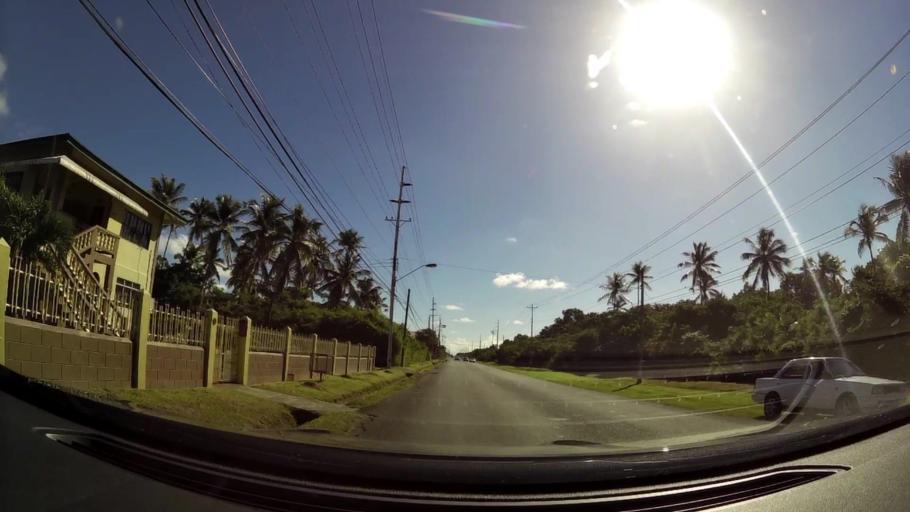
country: TT
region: Tobago
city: Scarborough
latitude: 11.1563
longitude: -60.8054
